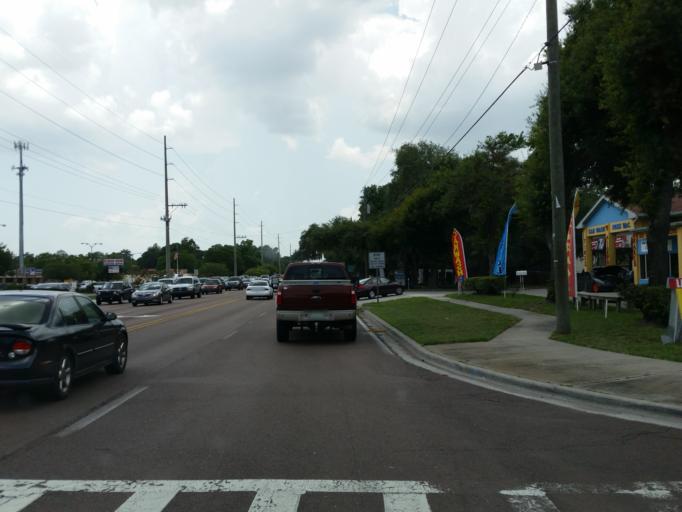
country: US
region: Florida
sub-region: Hillsborough County
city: Riverview
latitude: 27.8937
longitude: -82.2941
